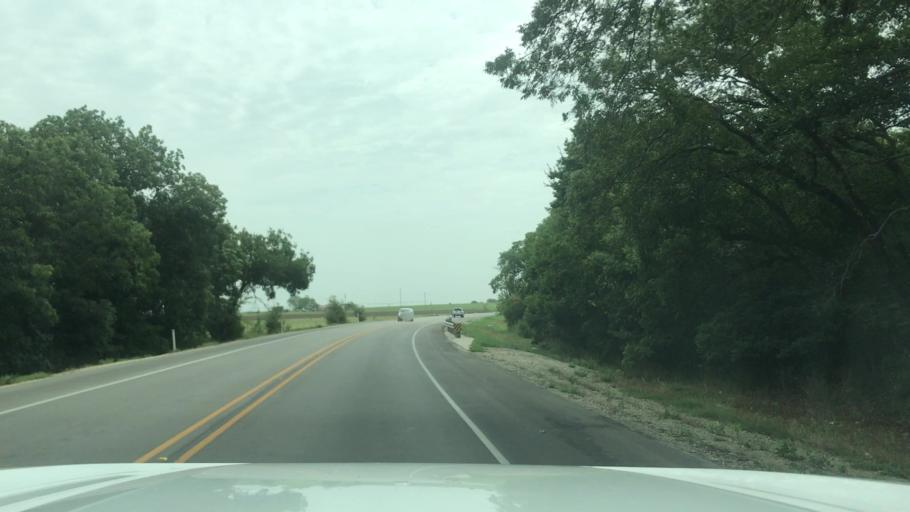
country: US
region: Texas
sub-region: Erath County
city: Dublin
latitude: 32.0920
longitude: -98.2681
